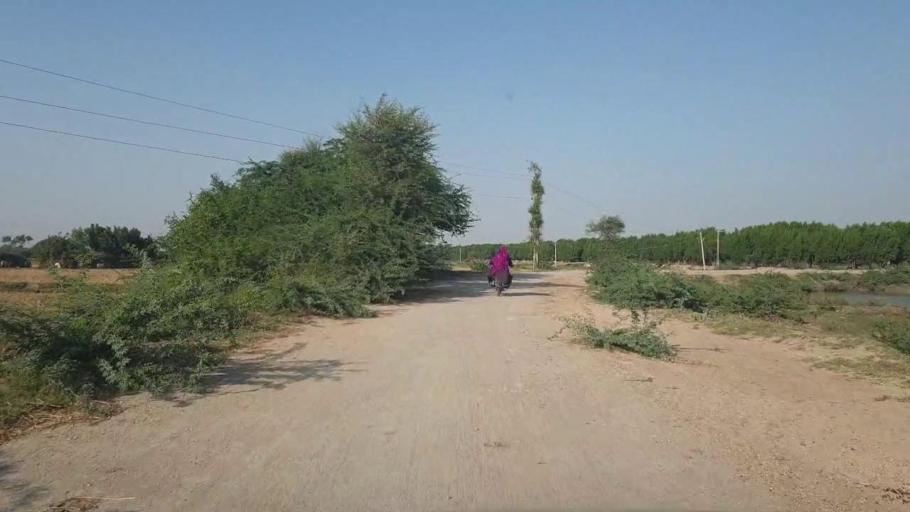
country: PK
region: Sindh
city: Badin
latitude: 24.6210
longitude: 68.8138
